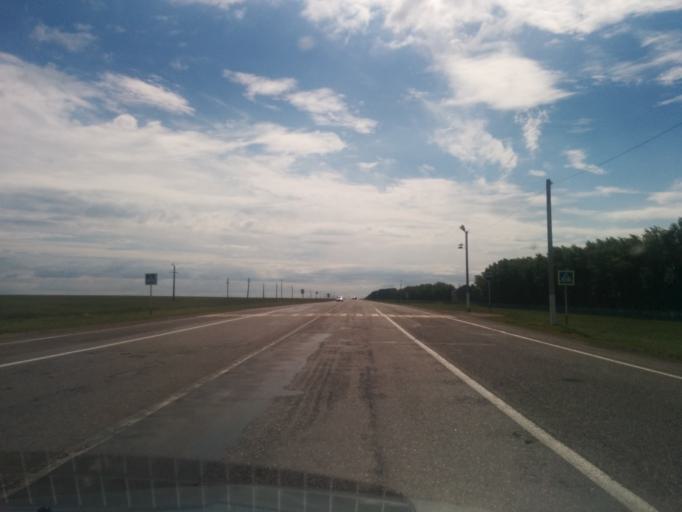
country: RU
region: Bashkortostan
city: Karmaskaly
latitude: 54.4253
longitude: 56.0333
